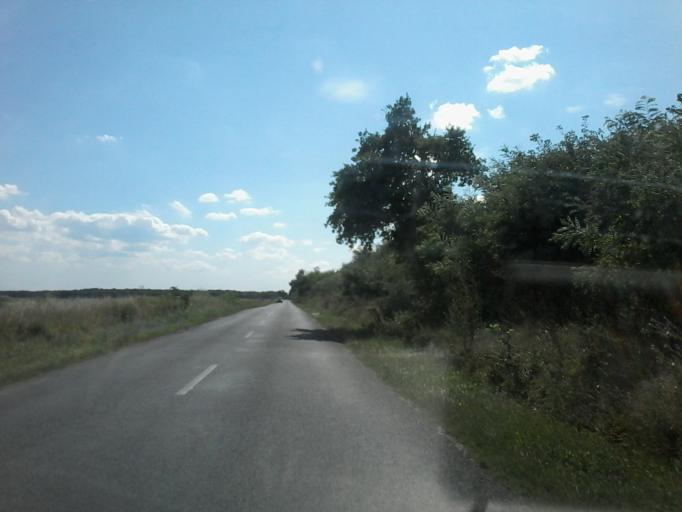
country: HU
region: Vas
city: Janoshaza
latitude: 47.0960
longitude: 17.1469
